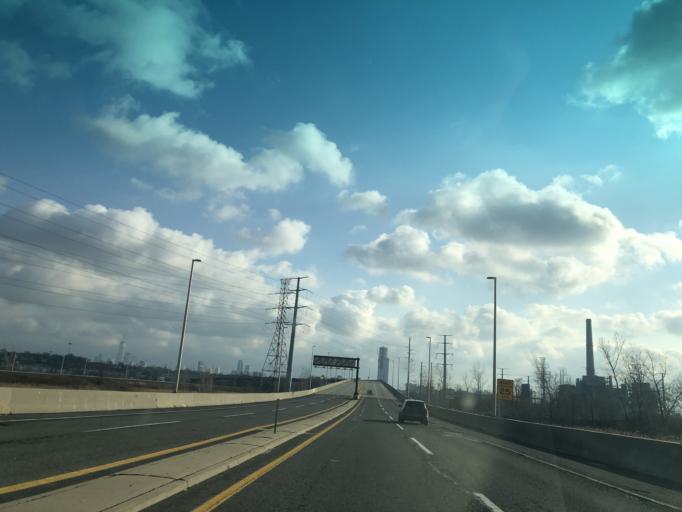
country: US
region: New Jersey
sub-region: Hudson County
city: Jersey City
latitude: 40.7557
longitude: -74.0731
